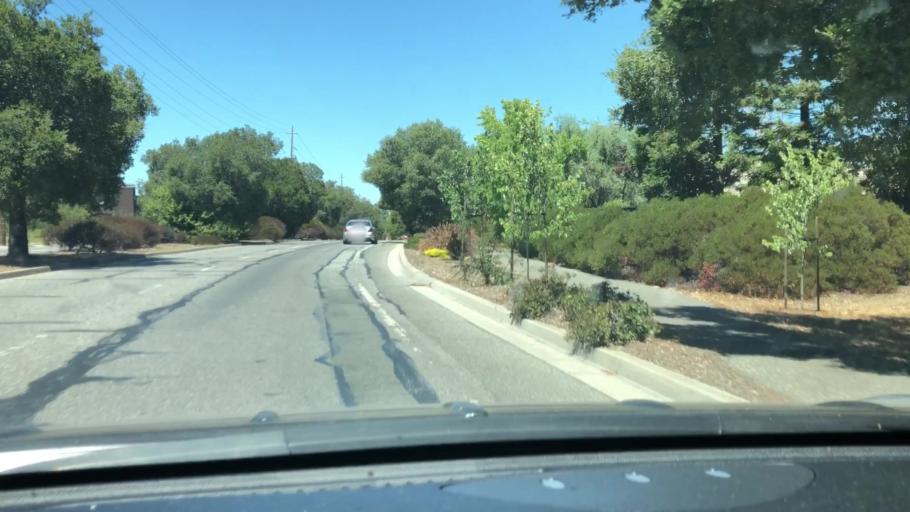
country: US
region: California
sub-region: Santa Clara County
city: Saratoga
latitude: 37.2685
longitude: -122.0139
